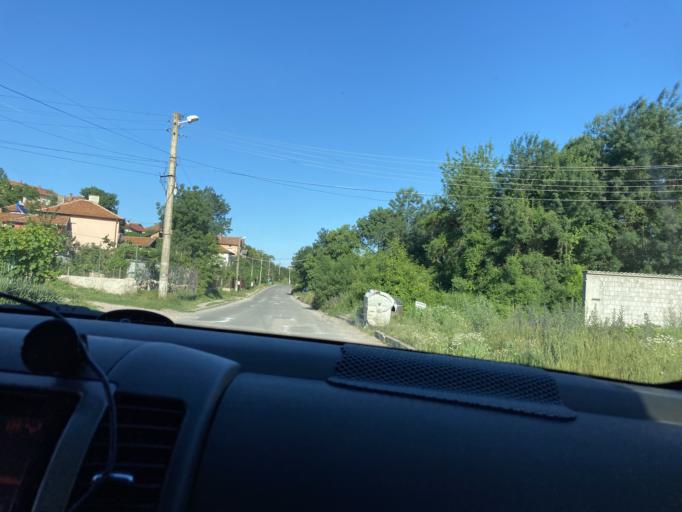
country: BG
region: Sofiya
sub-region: Obshtina Slivnitsa
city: Slivnitsa
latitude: 42.8469
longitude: 22.9910
